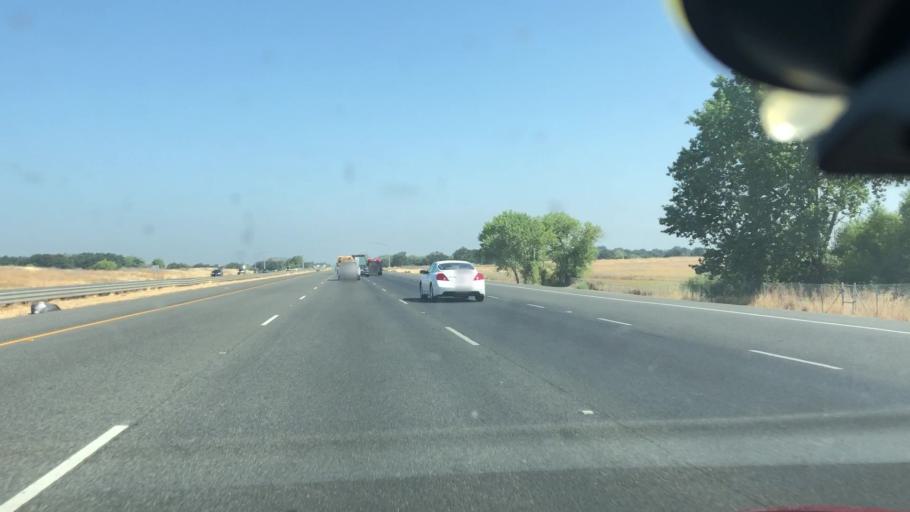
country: US
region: California
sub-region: Sacramento County
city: Laguna
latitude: 38.4320
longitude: -121.4881
